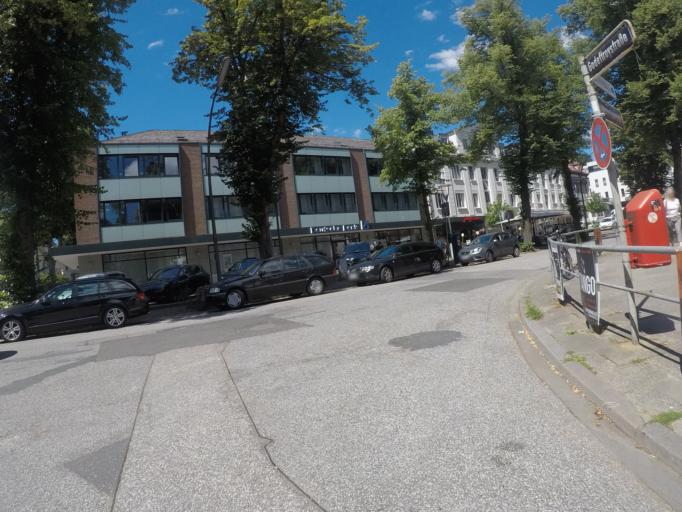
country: DE
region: Schleswig-Holstein
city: Halstenbek
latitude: 53.5624
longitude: 9.8123
